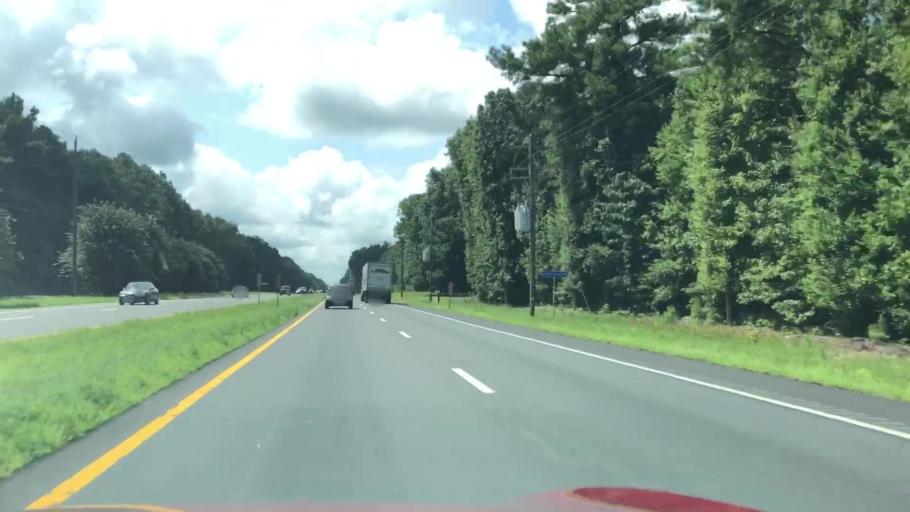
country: US
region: Virginia
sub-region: Northampton County
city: Exmore
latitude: 37.5039
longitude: -75.8395
